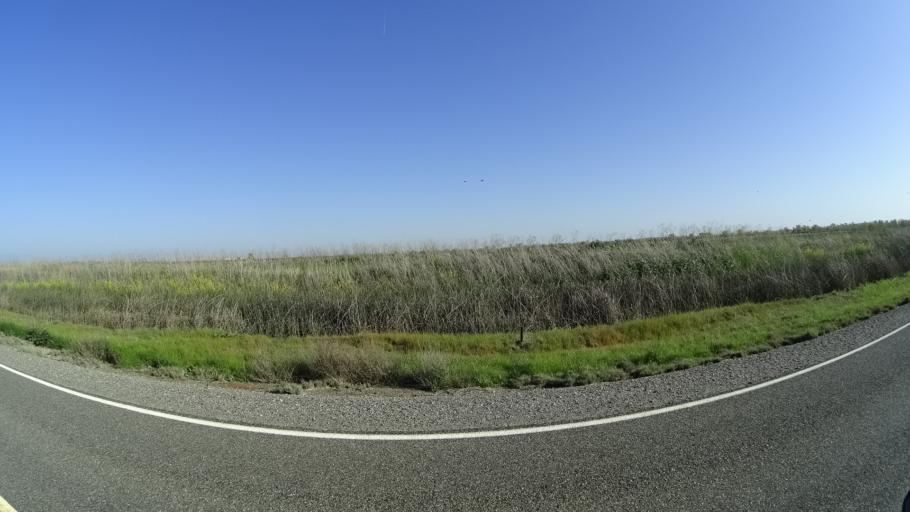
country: US
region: California
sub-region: Glenn County
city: Willows
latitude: 39.4074
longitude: -122.1509
